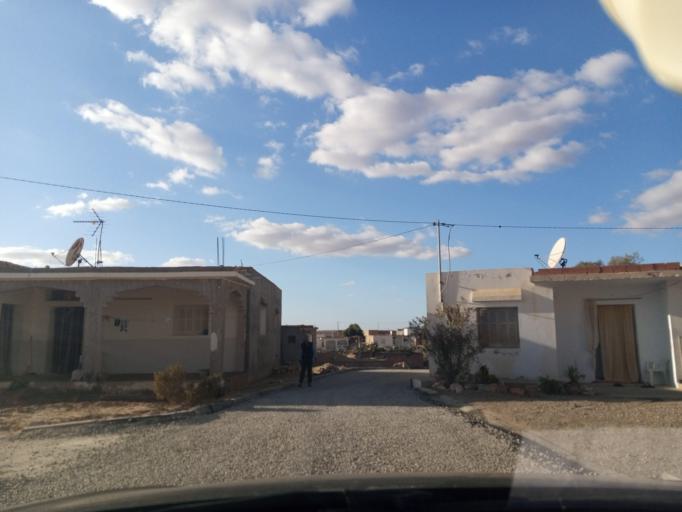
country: TN
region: Safaqis
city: Bi'r `Ali Bin Khalifah
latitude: 34.7102
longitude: 10.4240
